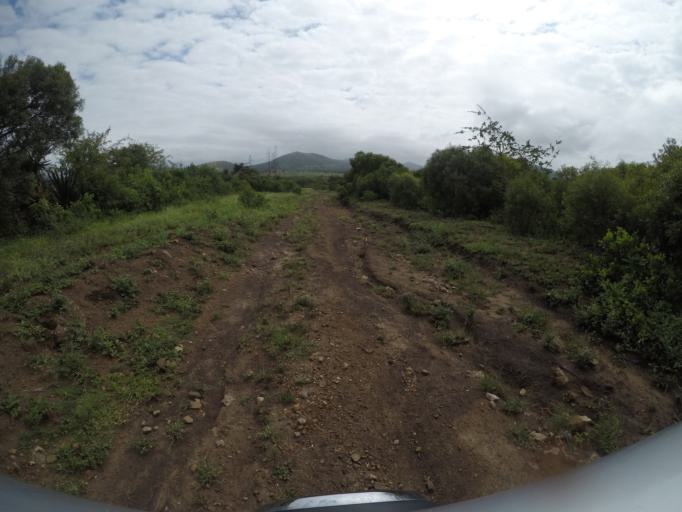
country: ZA
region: KwaZulu-Natal
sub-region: uThungulu District Municipality
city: Empangeni
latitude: -28.6247
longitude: 31.8646
